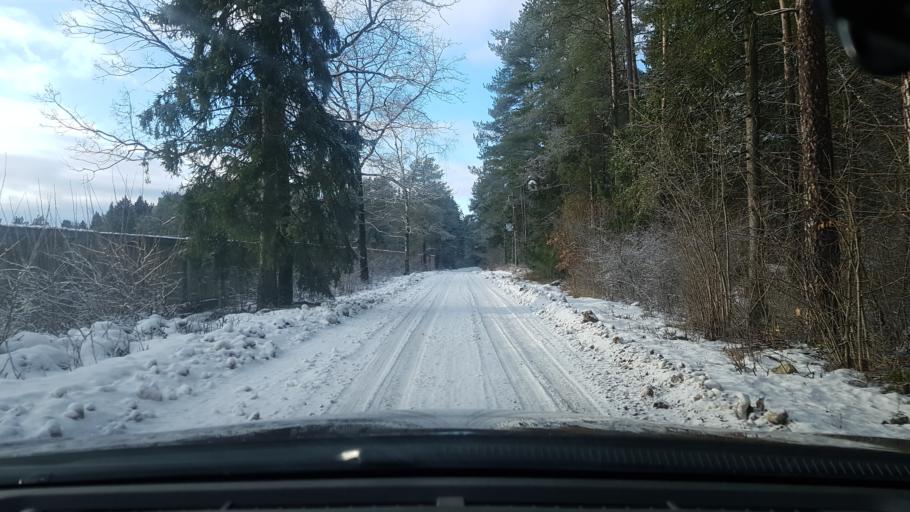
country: EE
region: Harju
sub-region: Keila linn
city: Keila
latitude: 59.2809
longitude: 24.2741
